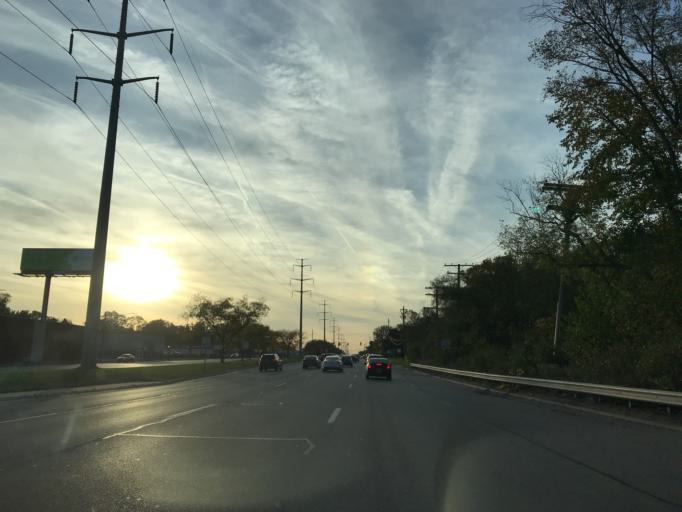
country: US
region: Michigan
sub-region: Wayne County
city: Redford
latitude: 42.4430
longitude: -83.2821
